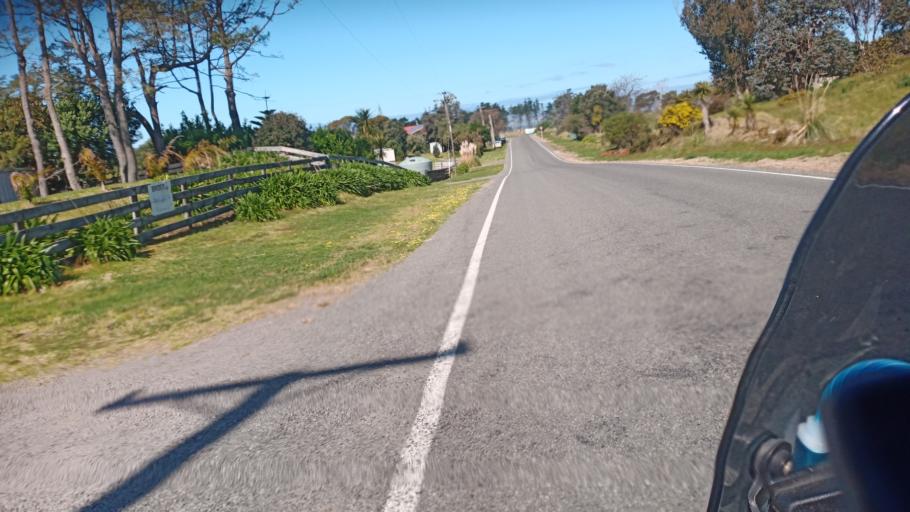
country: NZ
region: Gisborne
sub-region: Gisborne District
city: Gisborne
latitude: -39.0161
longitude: 177.8804
